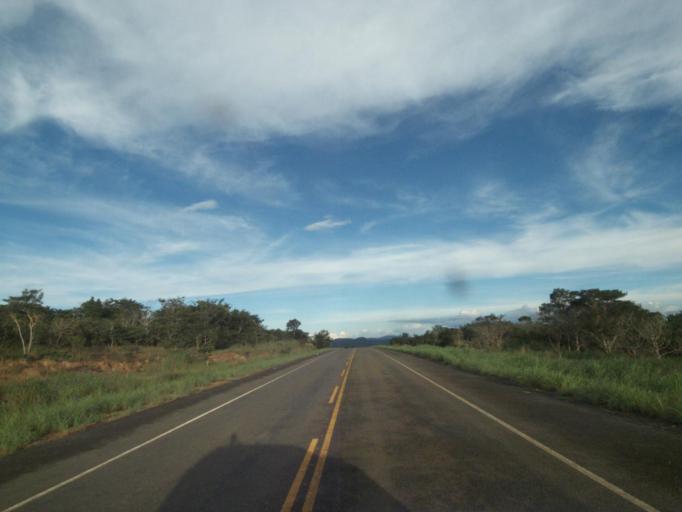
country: BR
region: Goias
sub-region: Jaragua
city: Jaragua
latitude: -15.8394
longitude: -49.2942
